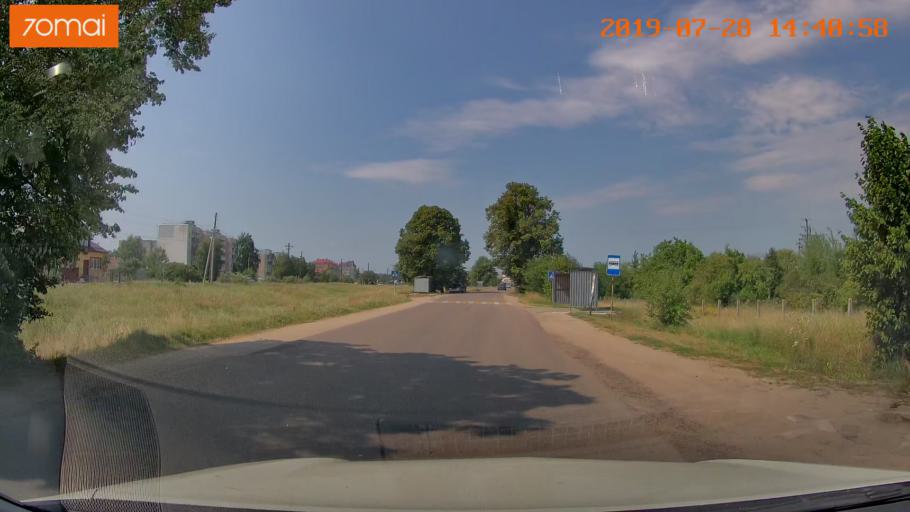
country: RU
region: Kaliningrad
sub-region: Gorod Kaliningrad
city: Yantarnyy
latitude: 54.8543
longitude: 19.9521
